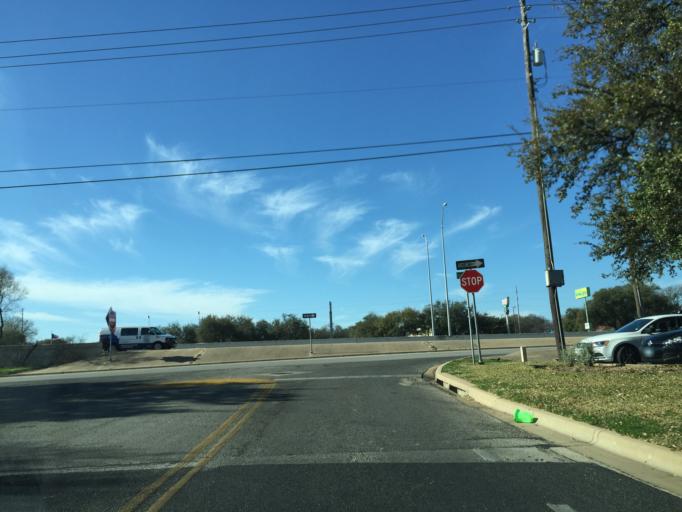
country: US
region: Texas
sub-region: Williamson County
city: Jollyville
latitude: 30.4311
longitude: -97.7615
